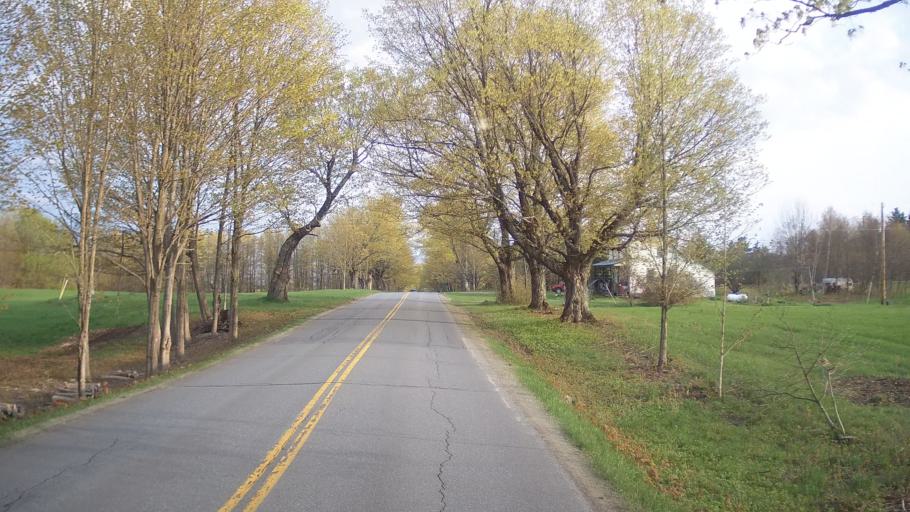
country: US
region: Vermont
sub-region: Orleans County
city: Newport
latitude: 44.9054
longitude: -72.4312
